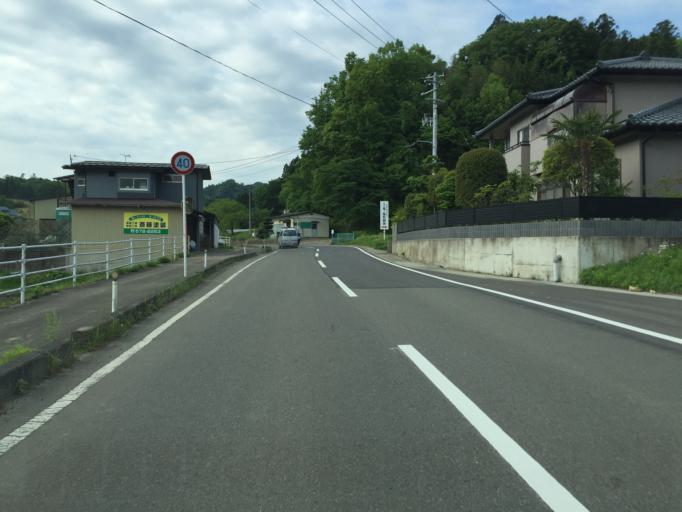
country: JP
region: Fukushima
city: Hobaramachi
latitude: 37.7233
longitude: 140.5946
